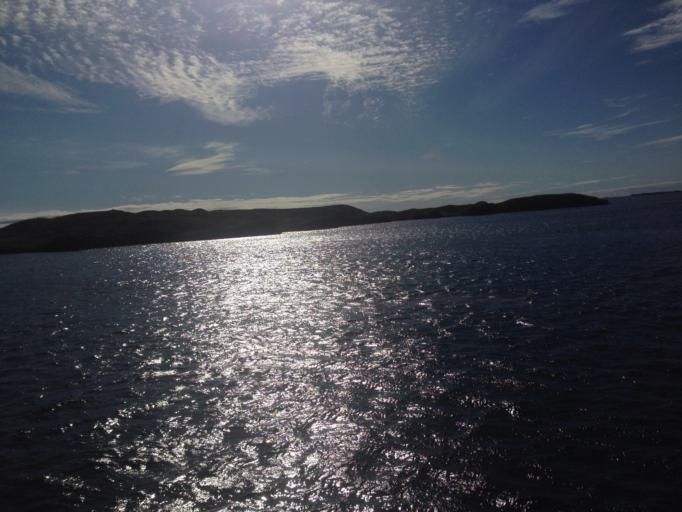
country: IS
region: West
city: Stykkisholmur
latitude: 65.1269
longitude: -22.5915
